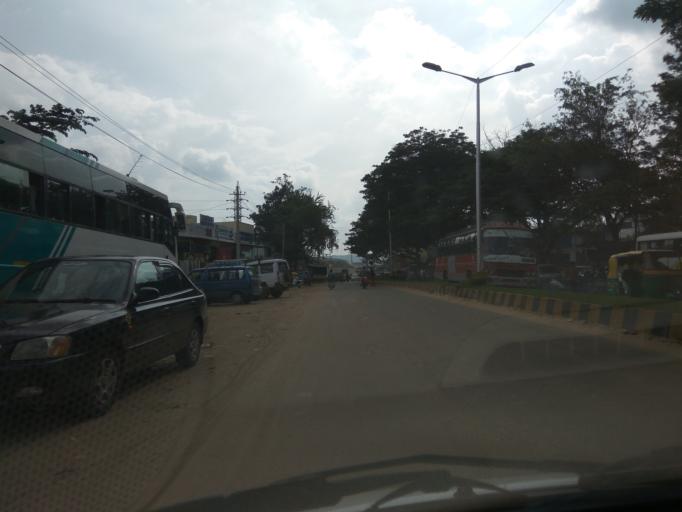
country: IN
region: Karnataka
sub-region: Kolar
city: Kolar
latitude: 13.1274
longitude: 78.1162
